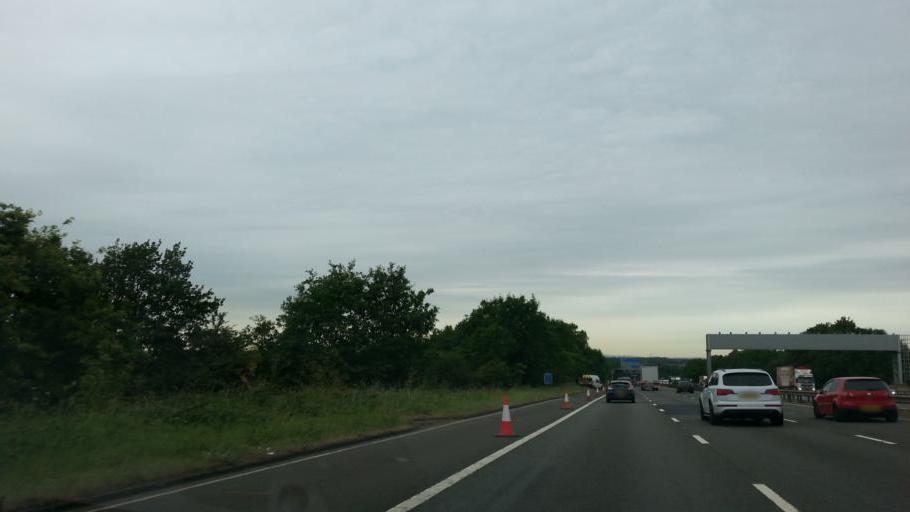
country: GB
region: England
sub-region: Solihull
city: Meriden
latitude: 52.4700
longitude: -1.6509
